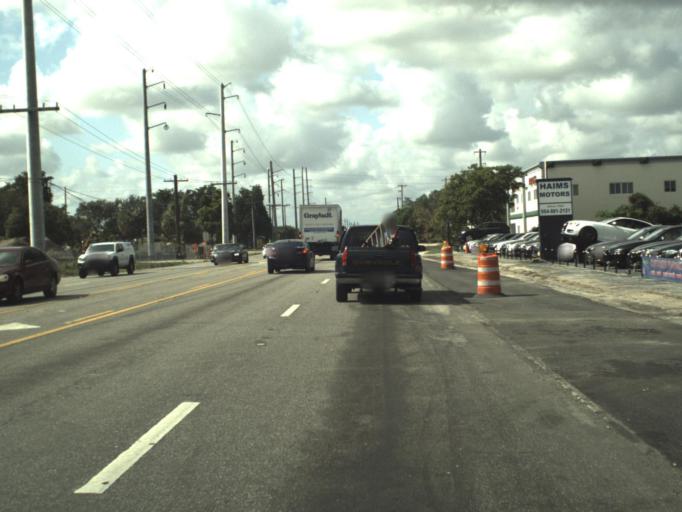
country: US
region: Florida
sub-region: Broward County
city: Pembroke Pines
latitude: 26.0357
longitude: -80.2086
